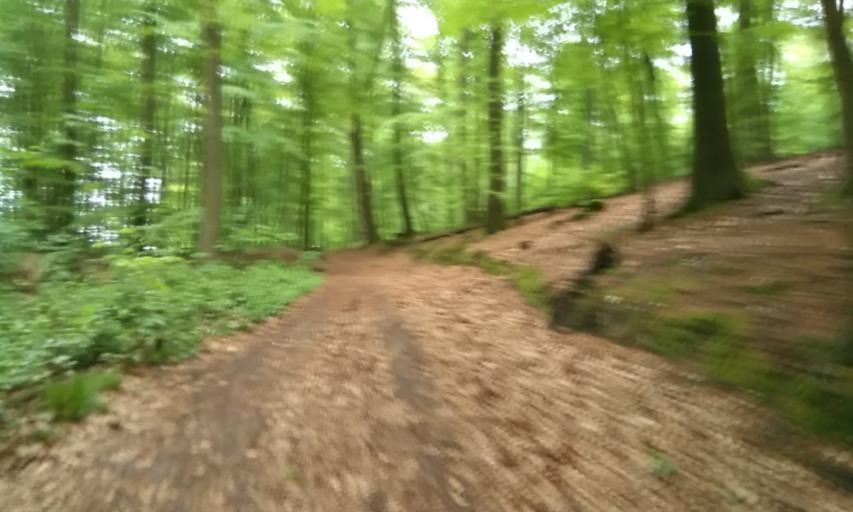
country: DE
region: Lower Saxony
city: Nottensdorf
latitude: 53.4792
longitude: 9.6317
